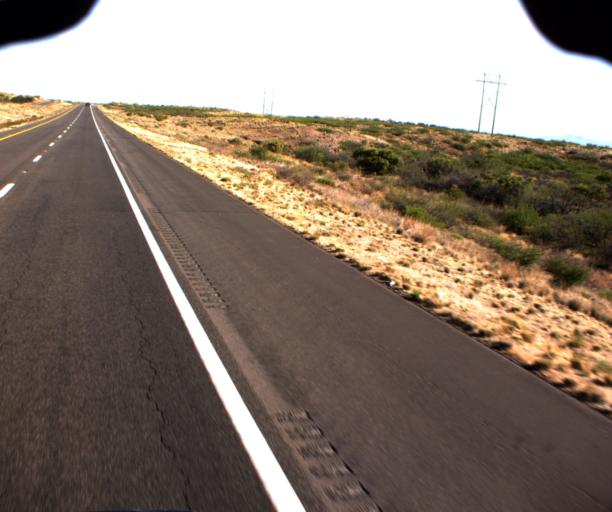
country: US
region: Arizona
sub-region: Graham County
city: Swift Trail Junction
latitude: 32.5107
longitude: -109.6738
